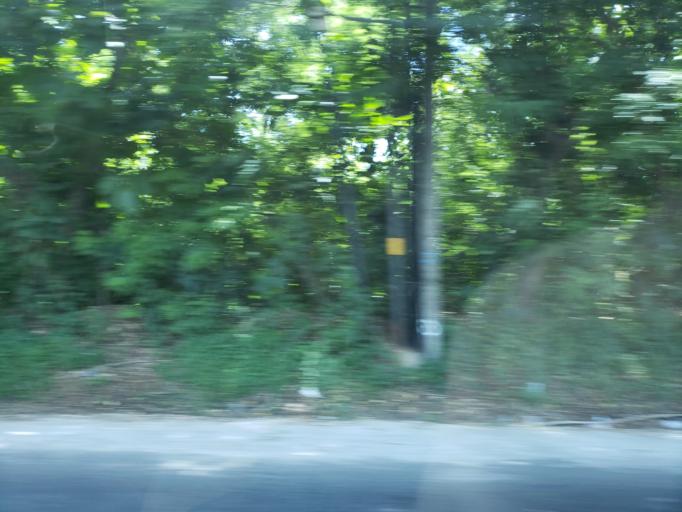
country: ID
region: Bali
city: Kangin
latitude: -8.8304
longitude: 115.1339
